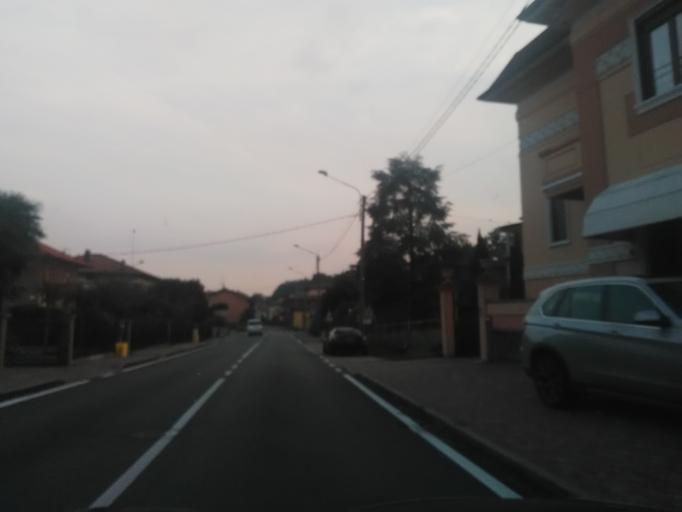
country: IT
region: Piedmont
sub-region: Provincia di Vercelli
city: San Maurizio
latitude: 45.6083
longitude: 8.2888
